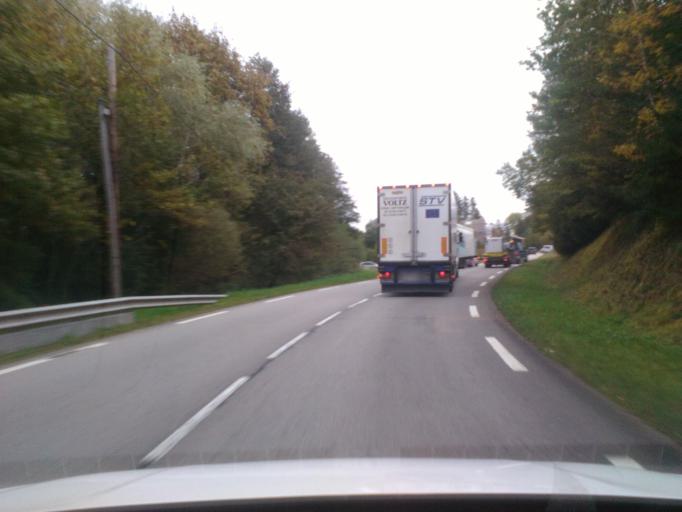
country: FR
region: Lorraine
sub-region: Departement des Vosges
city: Ban-de-Laveline
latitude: 48.3401
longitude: 7.1039
